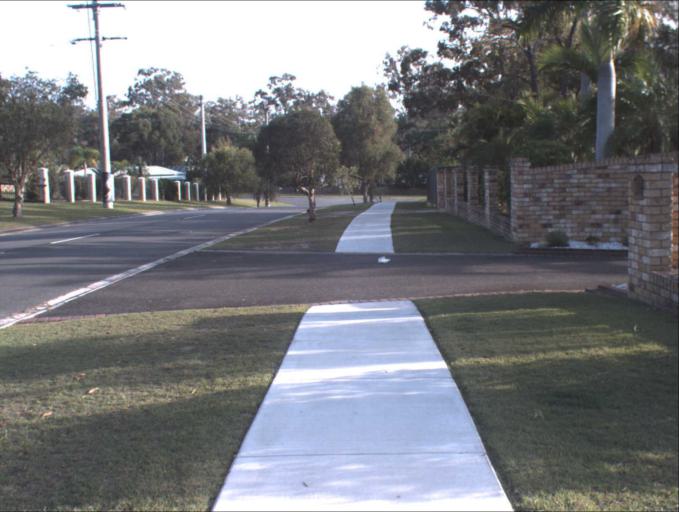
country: AU
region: Queensland
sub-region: Logan
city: Park Ridge South
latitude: -27.6764
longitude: 153.0135
